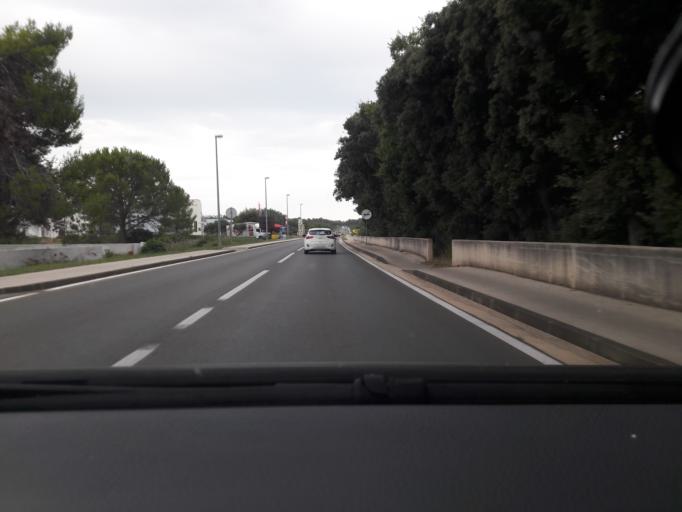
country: HR
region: Zadarska
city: Nin
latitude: 44.2143
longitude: 15.1785
